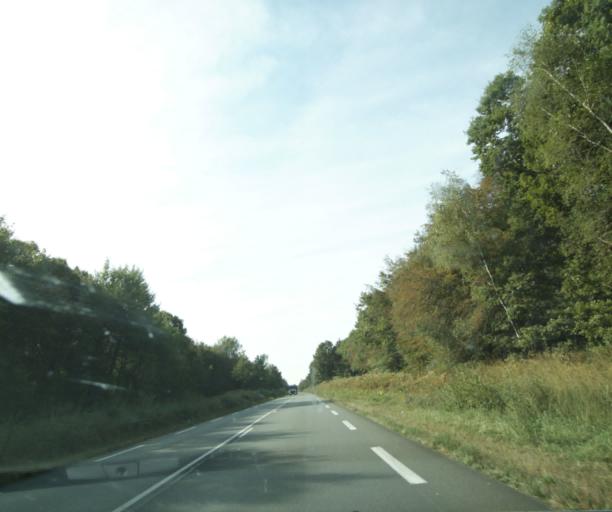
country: FR
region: Bourgogne
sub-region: Departement de Saone-et-Loire
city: Palinges
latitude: 46.5391
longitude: 4.1714
